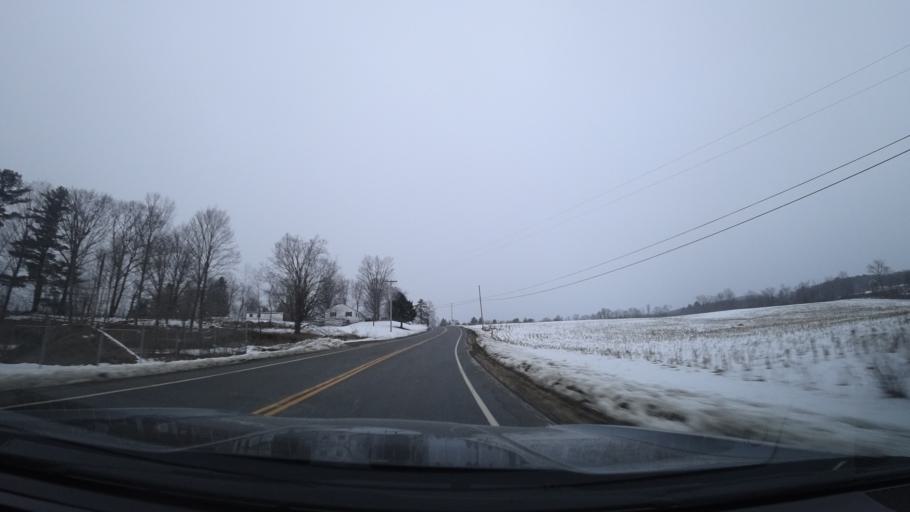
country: US
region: New York
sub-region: Washington County
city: Greenwich
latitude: 43.1418
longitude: -73.4167
